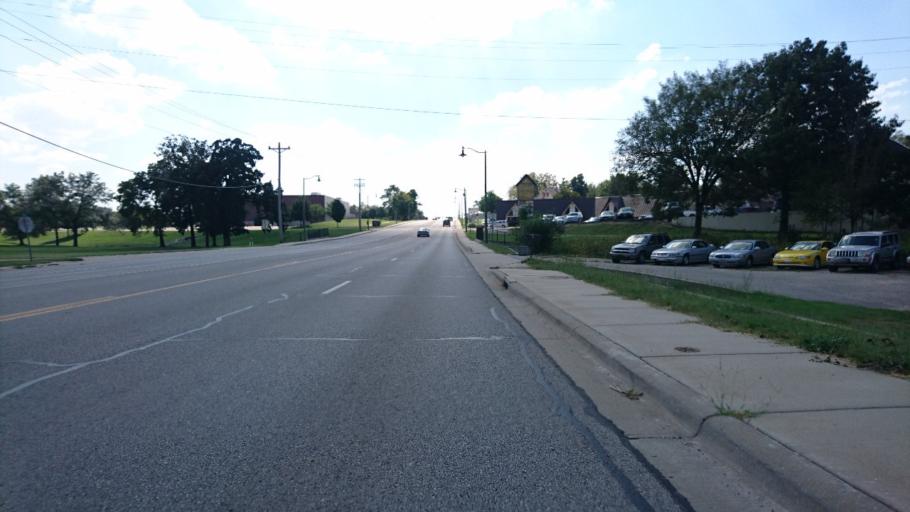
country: US
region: Missouri
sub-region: Laclede County
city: Lebanon
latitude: 37.6818
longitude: -92.6519
